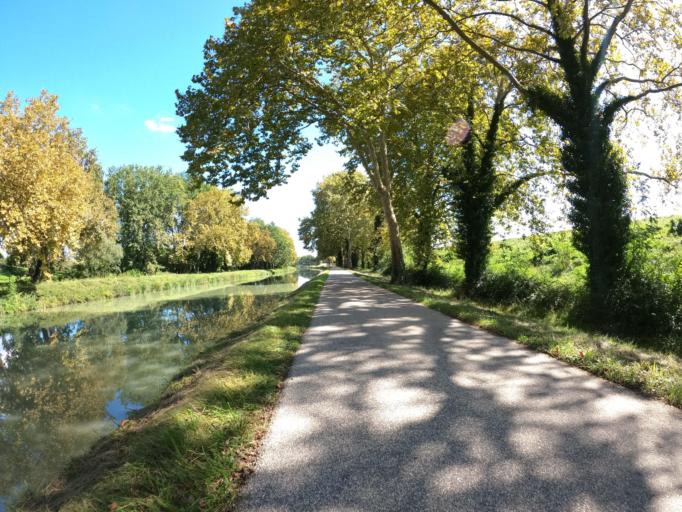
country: FR
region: Midi-Pyrenees
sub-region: Departement du Tarn-et-Garonne
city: Valence
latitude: 44.1009
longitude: 0.9123
